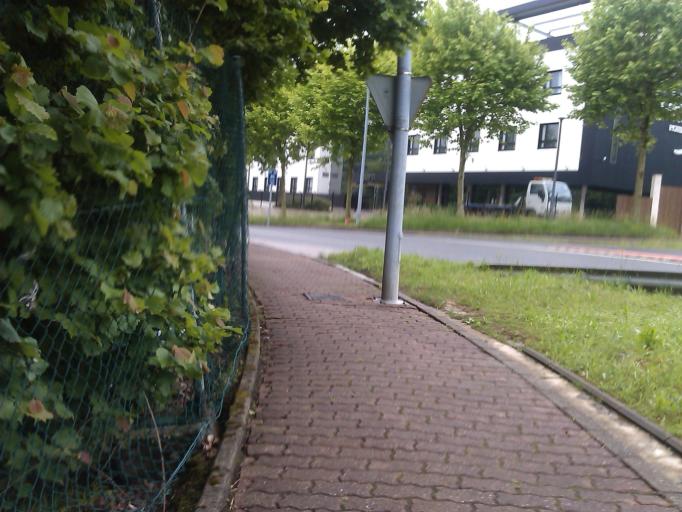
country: ES
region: Basque Country
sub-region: Provincia de Guipuzcoa
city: Urnieta
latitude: 43.2404
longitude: -1.9957
